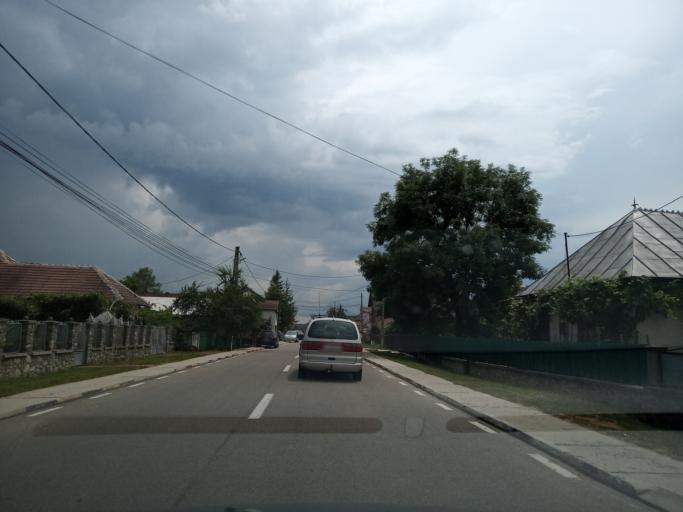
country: RO
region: Gorj
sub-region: Comuna Tismana
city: Tismana
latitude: 45.0517
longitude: 22.9464
